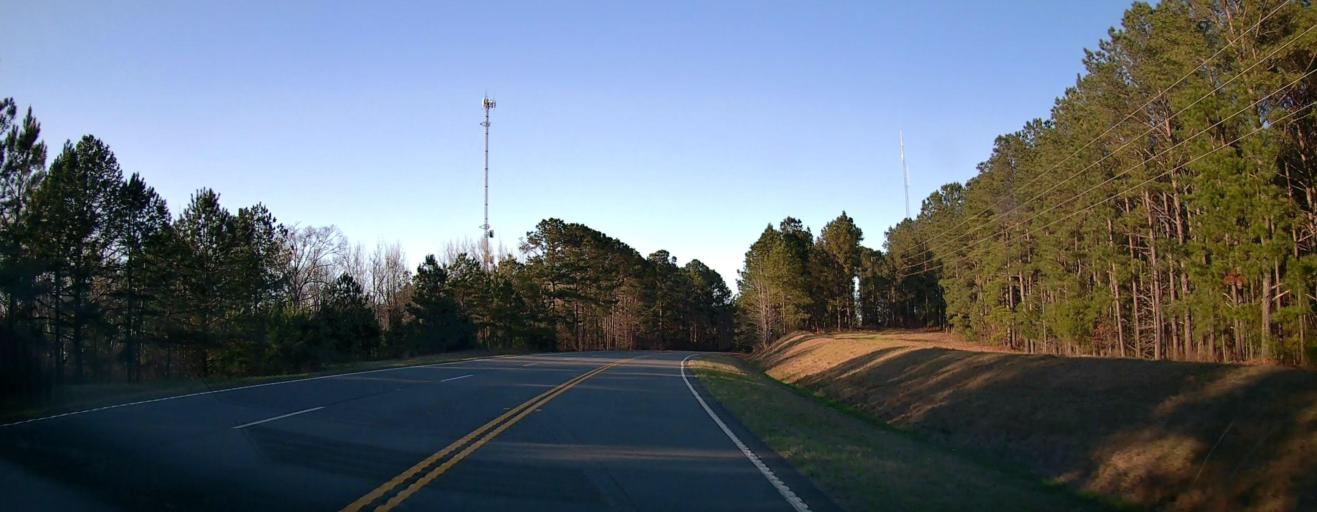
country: US
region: Georgia
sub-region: Talbot County
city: Talbotton
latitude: 32.6469
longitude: -84.5398
